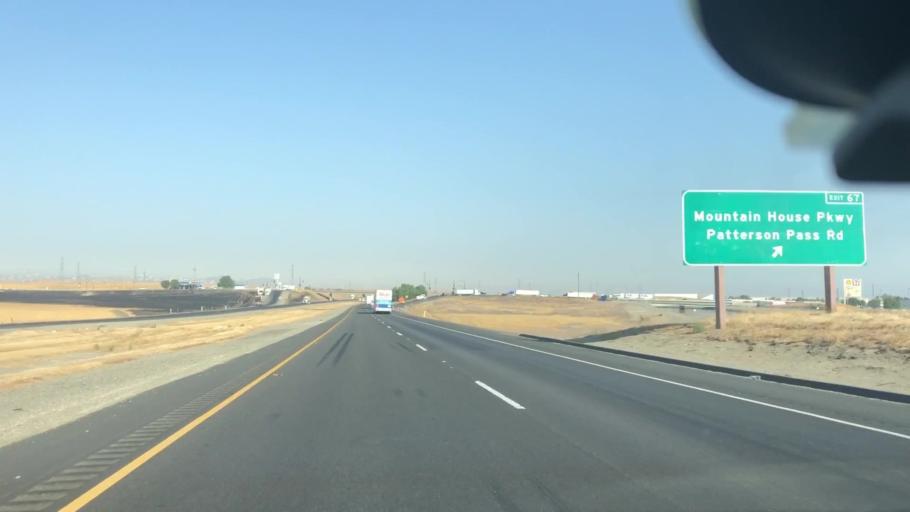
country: US
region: California
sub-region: San Joaquin County
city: Mountain House
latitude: 37.7175
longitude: -121.5298
